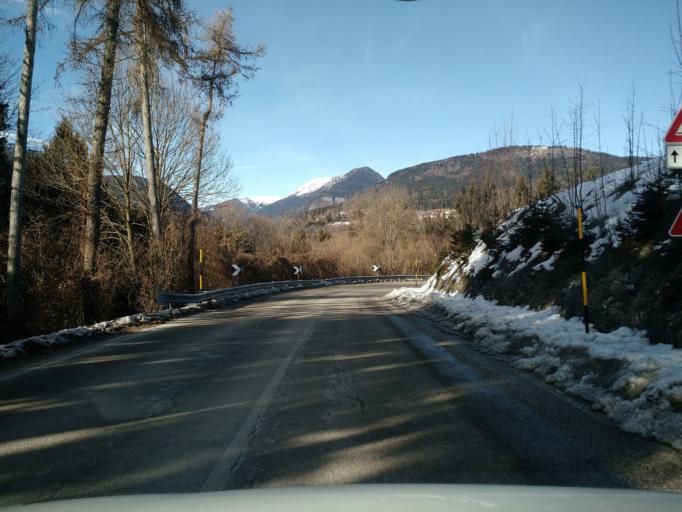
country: IT
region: Veneto
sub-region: Provincia di Vicenza
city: Canove di Roana
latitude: 45.8721
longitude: 11.4762
